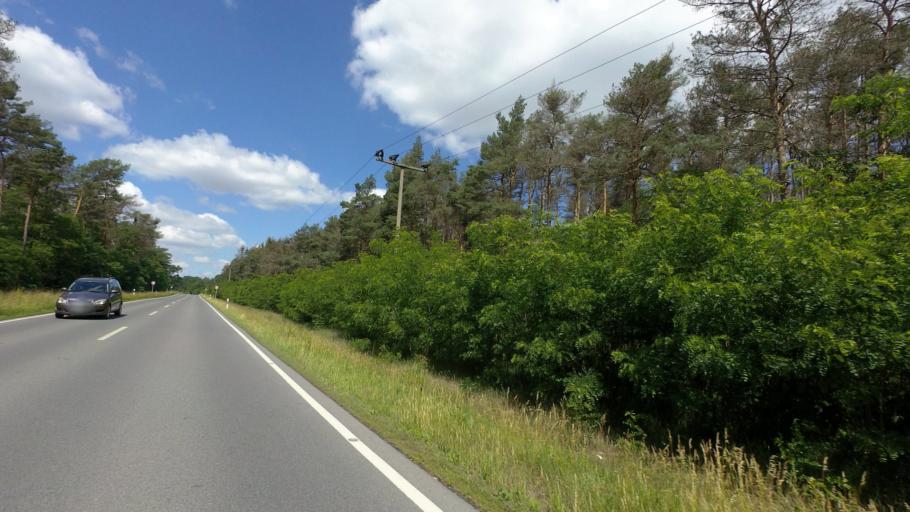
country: DE
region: Brandenburg
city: Finsterwalde
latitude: 51.6352
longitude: 13.7522
